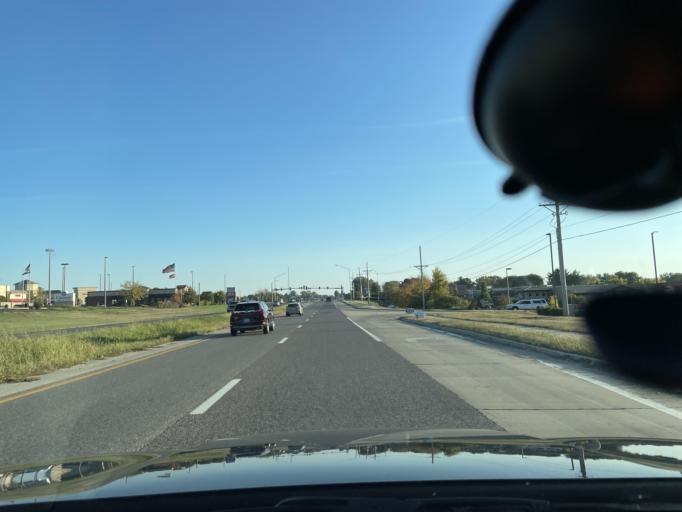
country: US
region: Missouri
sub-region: Andrew County
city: Country Club Village
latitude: 39.8161
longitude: -94.8153
